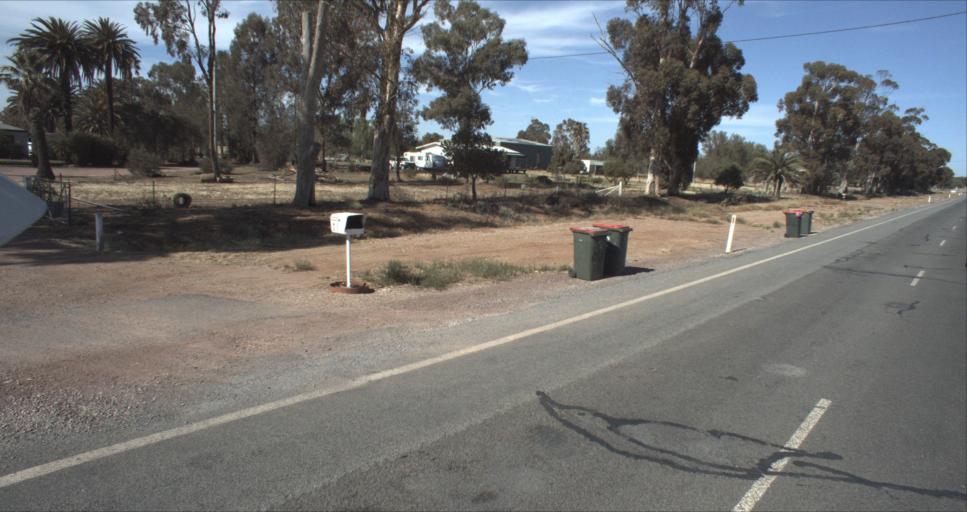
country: AU
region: New South Wales
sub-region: Leeton
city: Leeton
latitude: -34.5617
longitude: 146.4341
